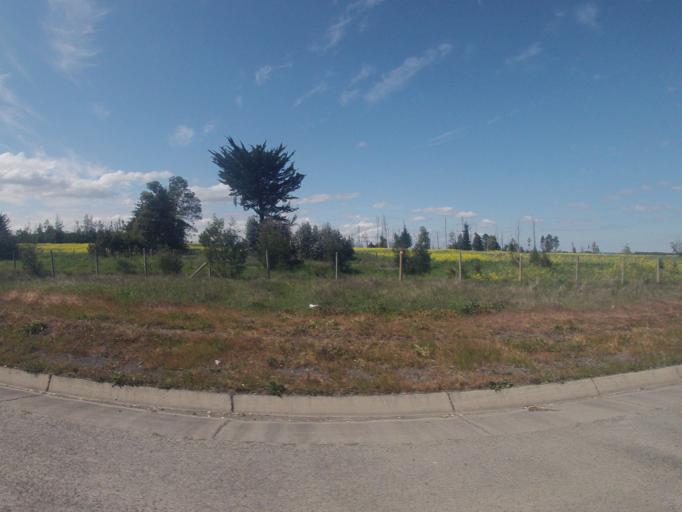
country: CL
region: Biobio
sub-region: Provincia de Biobio
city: Los Angeles
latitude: -37.4478
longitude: -72.4054
